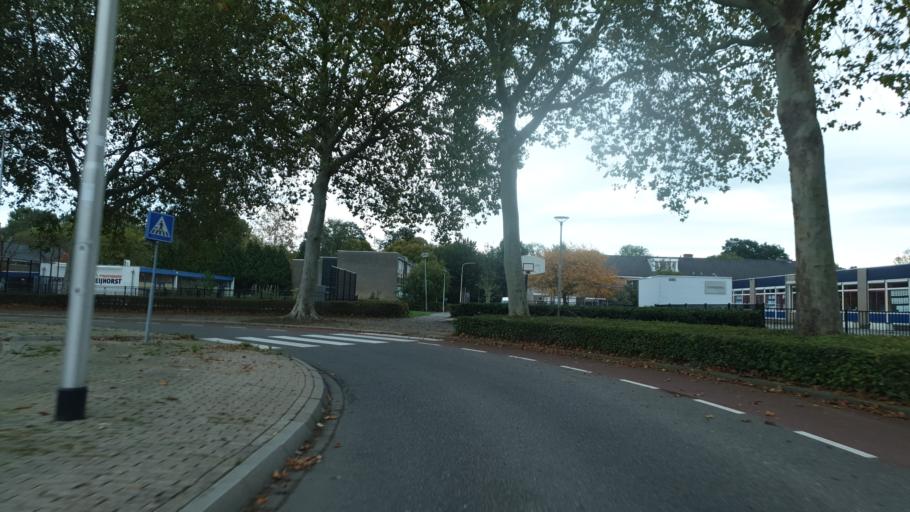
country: NL
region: Gelderland
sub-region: Gemeente Nijmegen
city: Lindenholt
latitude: 51.8130
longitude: 5.8092
